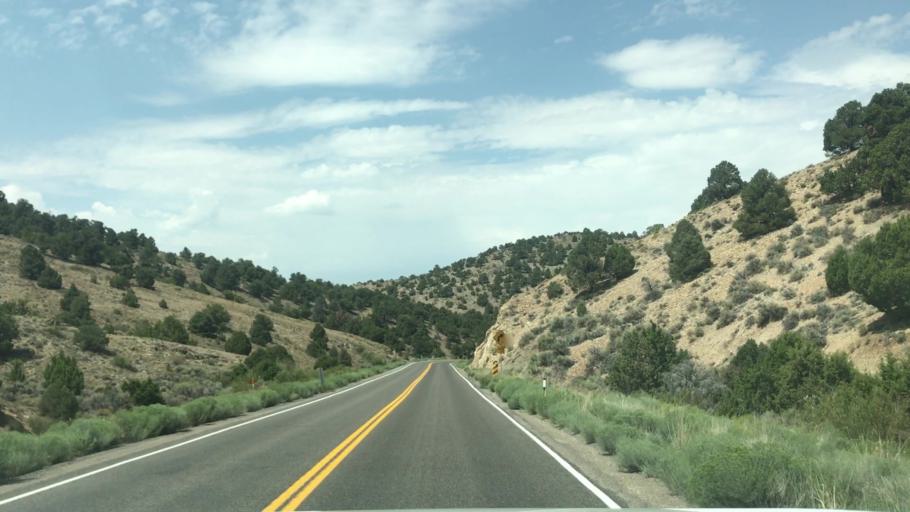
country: US
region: Nevada
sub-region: Eureka County
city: Eureka
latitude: 39.3949
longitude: -115.4819
